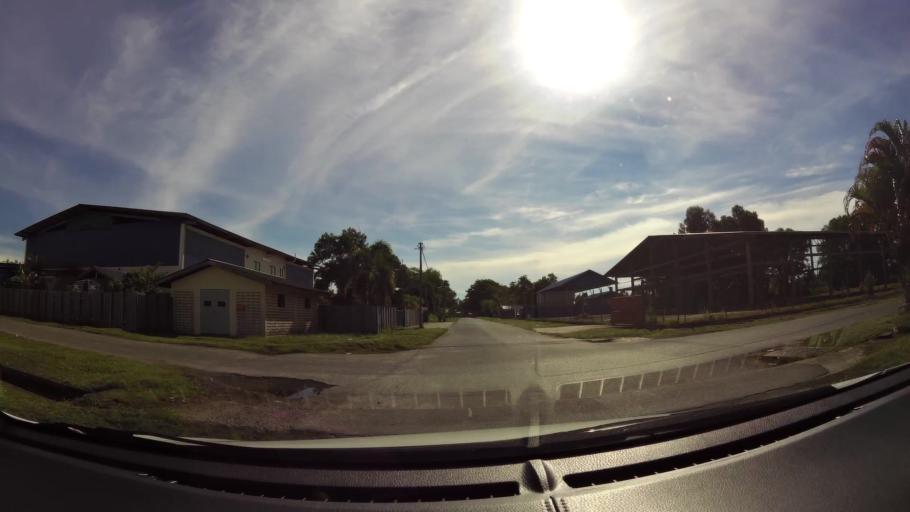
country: BN
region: Belait
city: Kuala Belait
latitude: 4.5726
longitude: 114.2049
